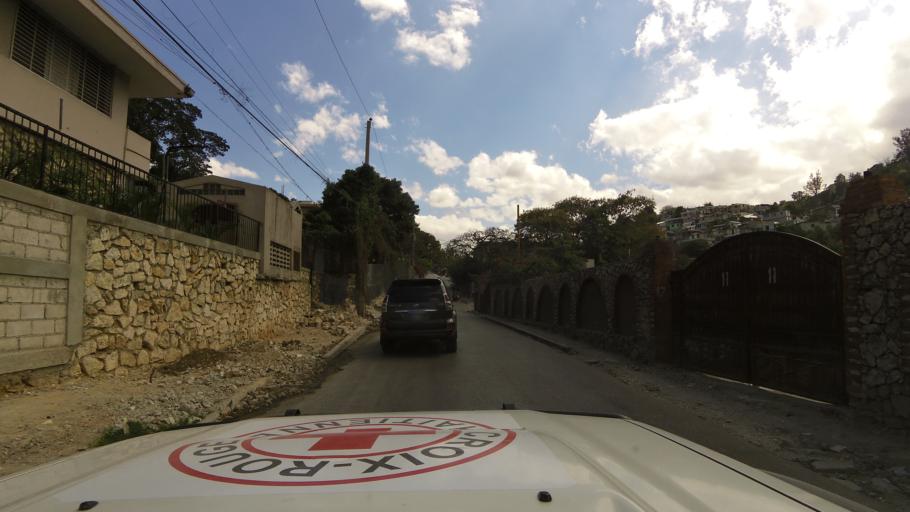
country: HT
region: Ouest
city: Delmas 73
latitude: 18.5299
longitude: -72.2929
